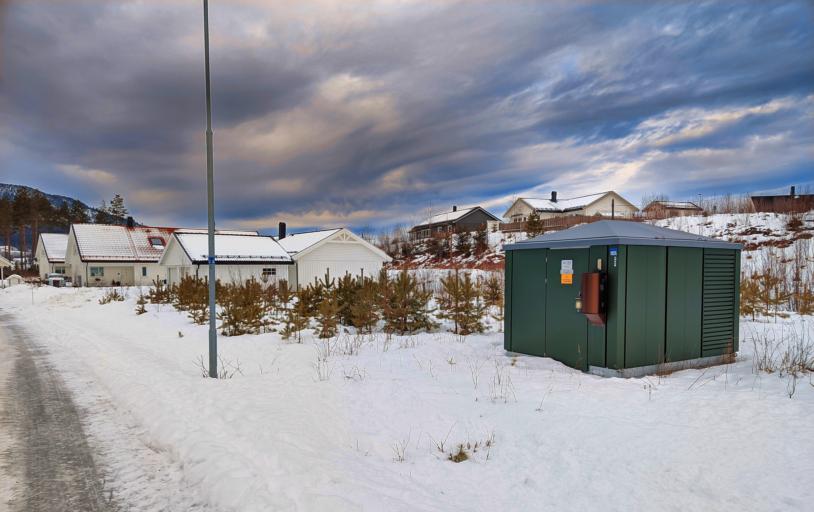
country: NO
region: Buskerud
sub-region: Kongsberg
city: Kongsberg
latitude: 59.5525
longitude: 9.8036
